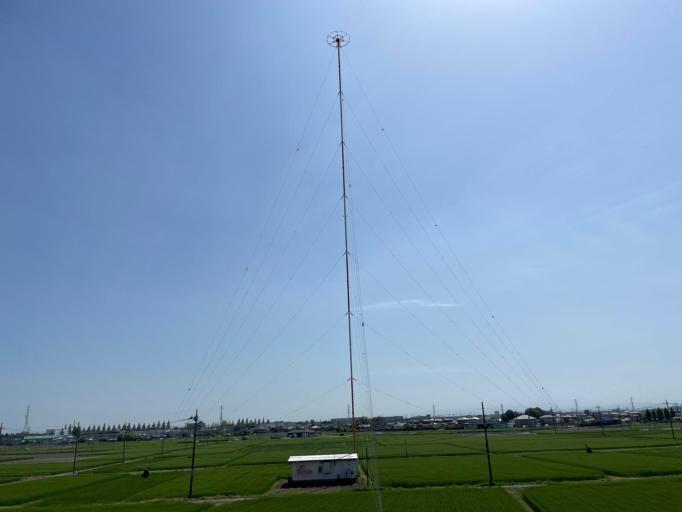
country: JP
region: Tochigi
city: Ashikaga
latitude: 36.3025
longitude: 139.4940
